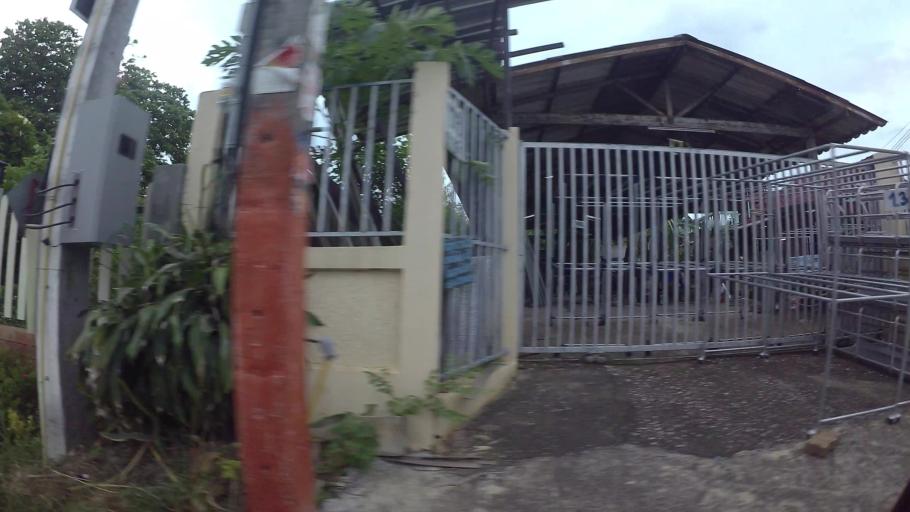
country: TH
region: Chon Buri
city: Sattahip
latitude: 12.6887
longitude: 100.8991
